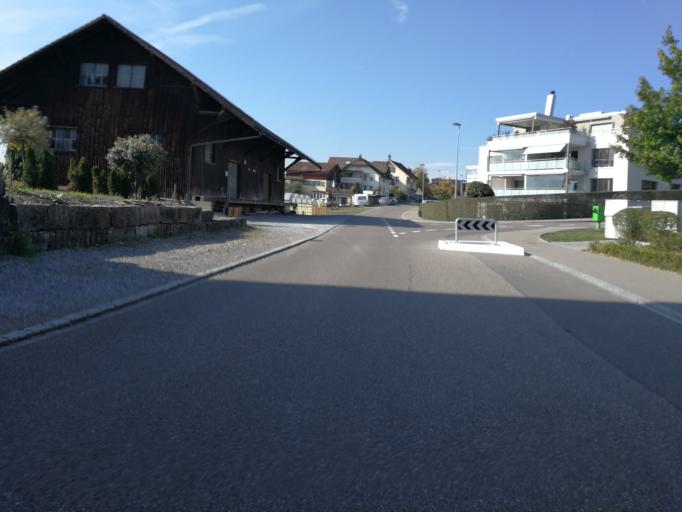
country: CH
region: Zurich
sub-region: Bezirk Hinwil
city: Tann / Tann (Dorfkern)
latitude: 47.2648
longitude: 8.8477
